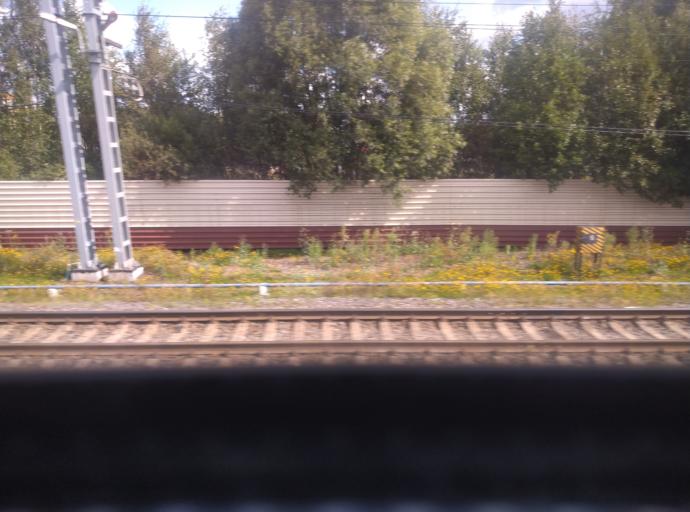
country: RU
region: St.-Petersburg
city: Kolpino
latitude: 59.7551
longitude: 30.6057
